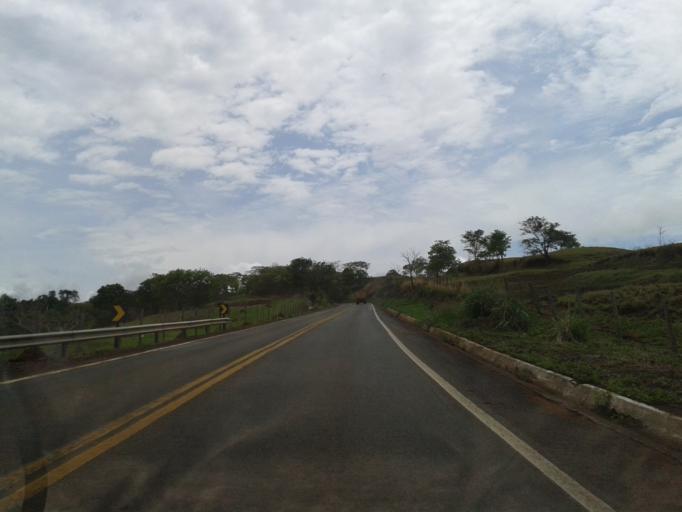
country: BR
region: Goias
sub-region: Buriti Alegre
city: Buriti Alegre
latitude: -18.1378
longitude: -48.9498
